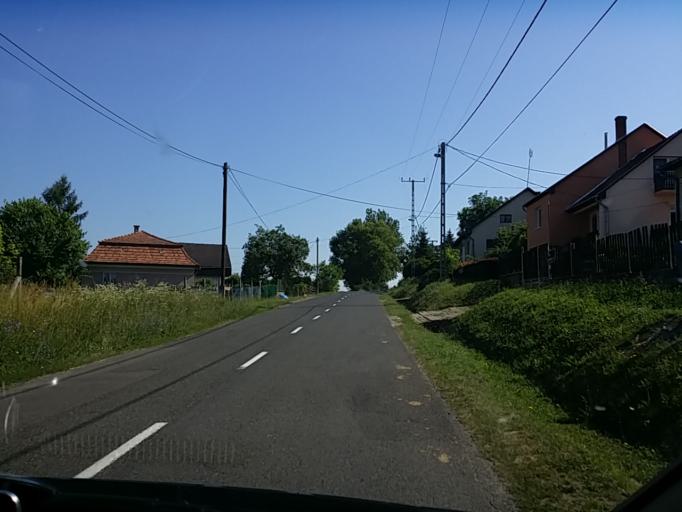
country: HU
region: Nograd
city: Karancskeszi
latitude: 48.2139
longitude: 19.5998
